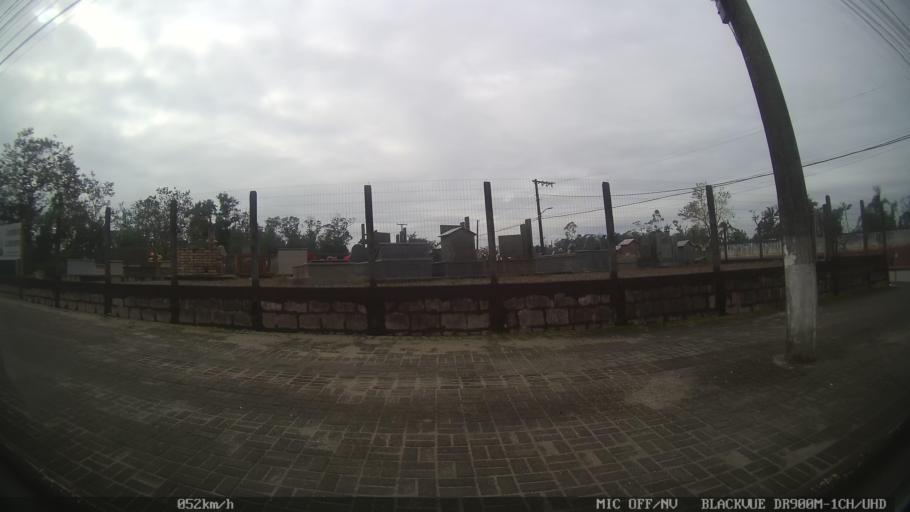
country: BR
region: Santa Catarina
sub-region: Joinville
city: Joinville
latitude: -26.0452
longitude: -48.8557
